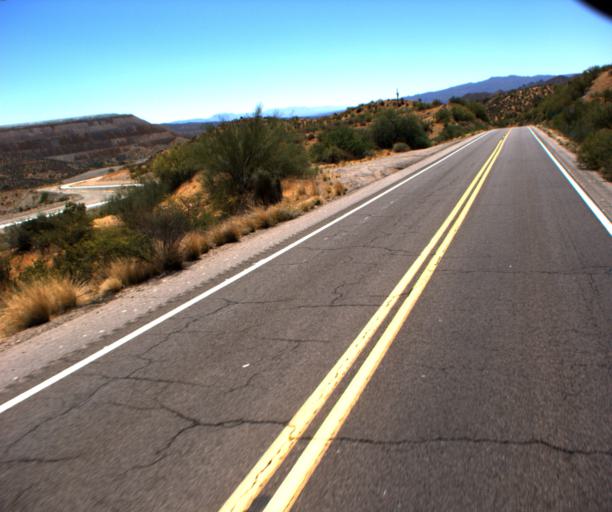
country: US
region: Arizona
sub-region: Pinal County
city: Kearny
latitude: 33.1349
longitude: -110.9884
